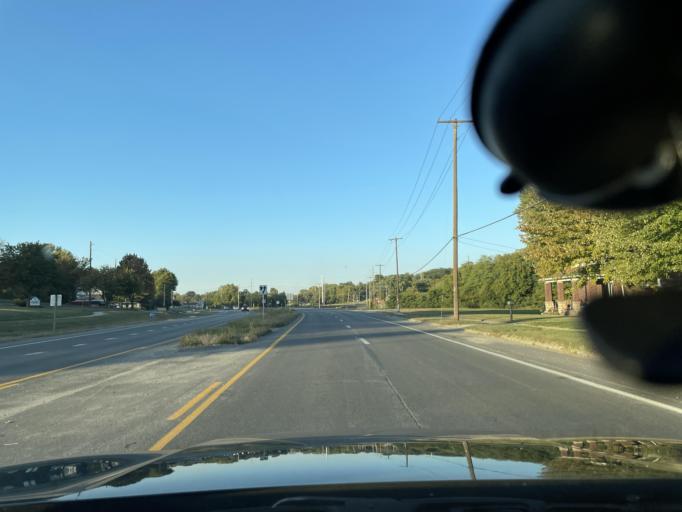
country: US
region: Missouri
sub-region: Buchanan County
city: Saint Joseph
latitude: 39.8034
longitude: -94.8422
